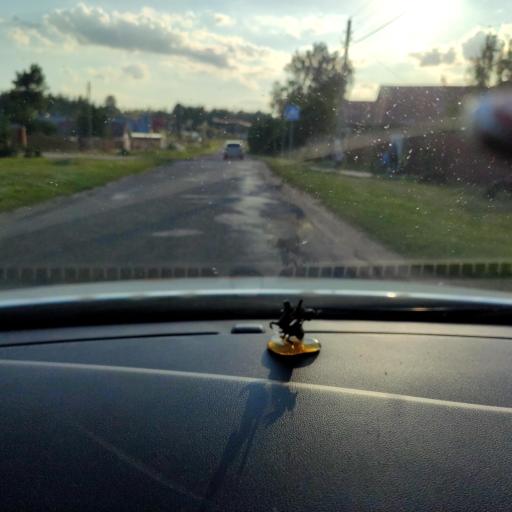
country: RU
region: Tatarstan
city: Pestretsy
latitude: 55.6158
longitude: 49.4944
